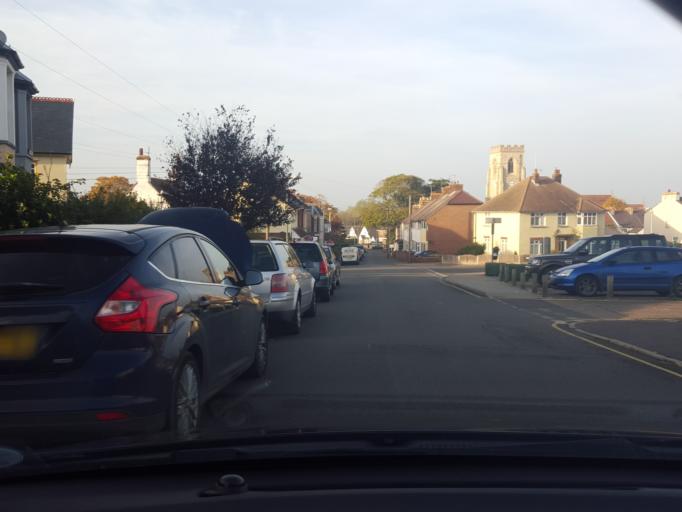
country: GB
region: England
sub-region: Essex
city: Walton-on-the-Naze
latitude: 51.8466
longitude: 1.2682
